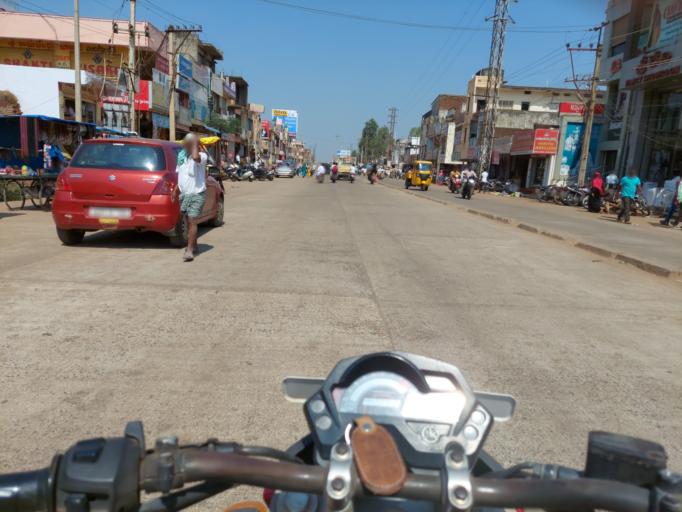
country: IN
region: Telangana
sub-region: Rangareddi
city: Vikarabad
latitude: 17.3377
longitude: 77.9049
